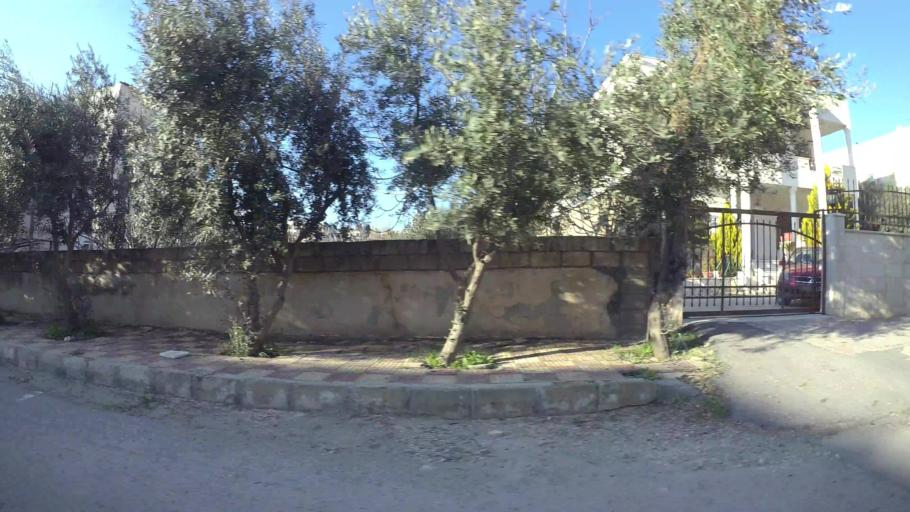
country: JO
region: Amman
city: Al Bunayyat ash Shamaliyah
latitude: 31.8965
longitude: 35.9114
